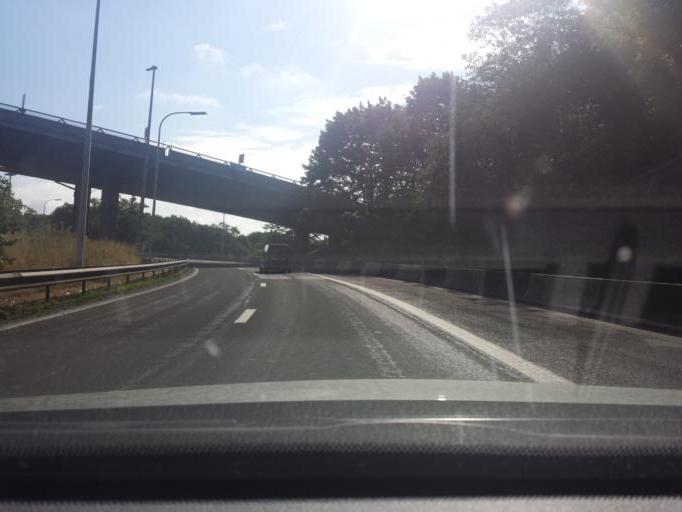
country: BE
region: Flanders
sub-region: Provincie Vlaams-Brabant
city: Diegem
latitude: 50.9010
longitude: 4.4341
